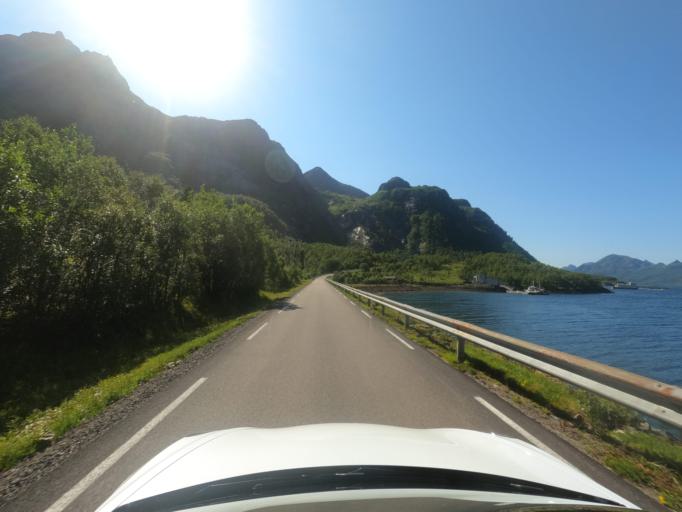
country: NO
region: Nordland
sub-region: Hadsel
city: Stokmarknes
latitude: 68.3447
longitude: 15.0509
